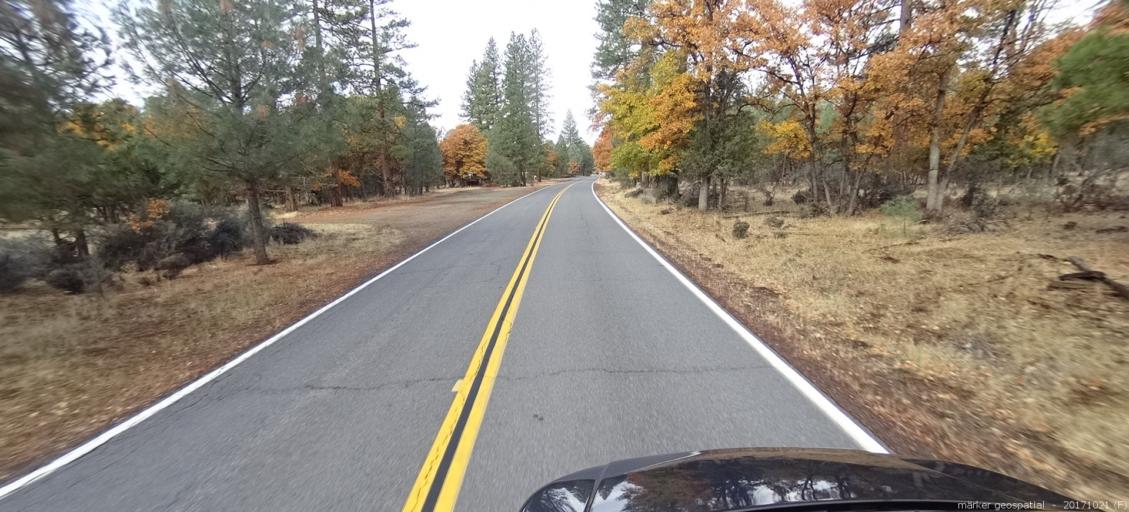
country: US
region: California
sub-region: Shasta County
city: Burney
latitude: 40.9184
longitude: -121.5457
